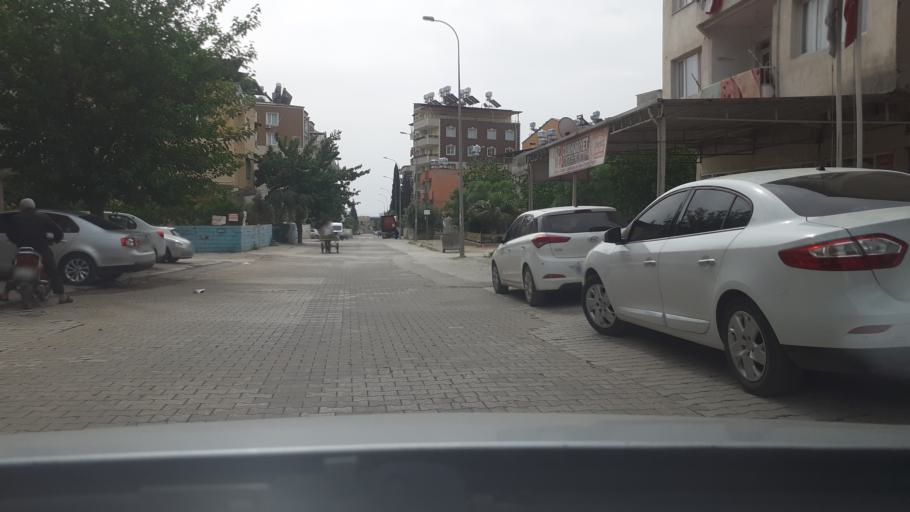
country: TR
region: Hatay
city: Kirikhan
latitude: 36.4960
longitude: 36.3623
